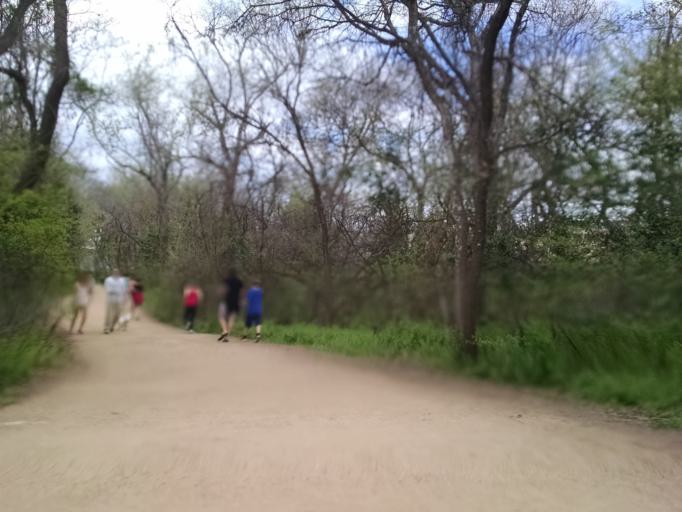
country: US
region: Texas
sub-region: Travis County
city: Rollingwood
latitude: 30.2727
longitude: -97.7693
